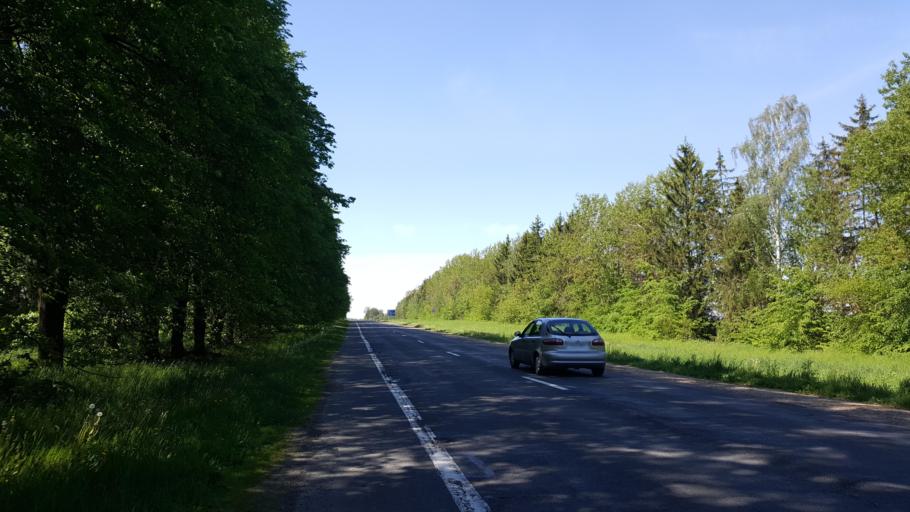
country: BY
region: Brest
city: Kamyanyets
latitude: 52.3746
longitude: 23.7992
